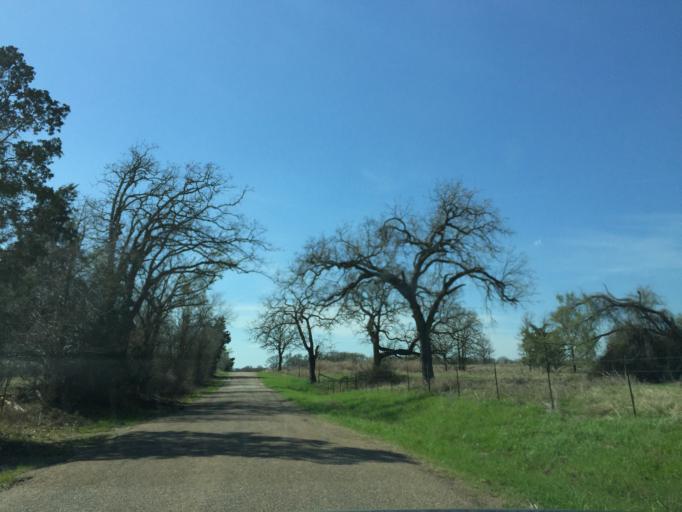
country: US
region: Texas
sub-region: Milam County
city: Thorndale
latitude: 30.5746
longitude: -97.1641
